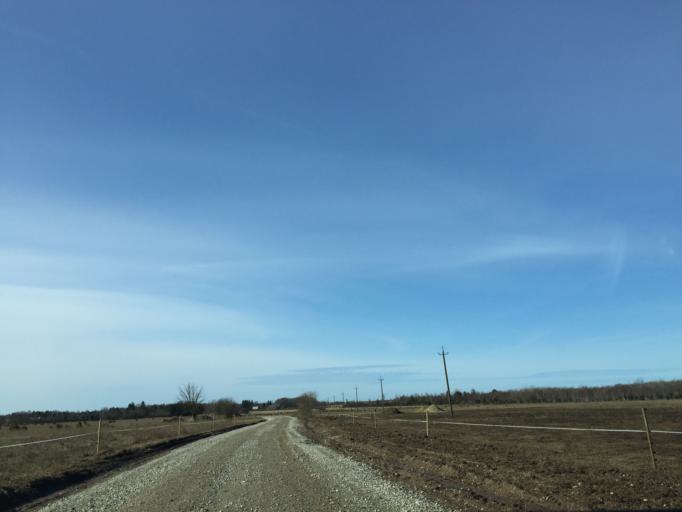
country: EE
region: Laeaene
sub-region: Haapsalu linn
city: Haapsalu
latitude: 58.6725
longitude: 23.5407
